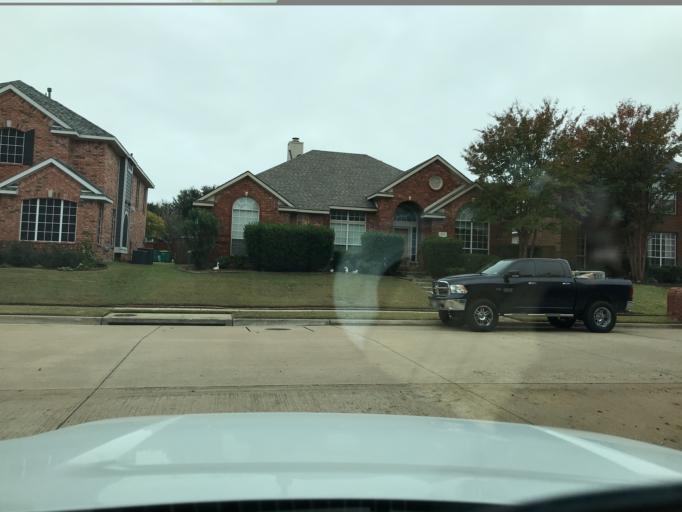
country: US
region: Texas
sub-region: Denton County
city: Highland Village
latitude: 33.0828
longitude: -97.0293
